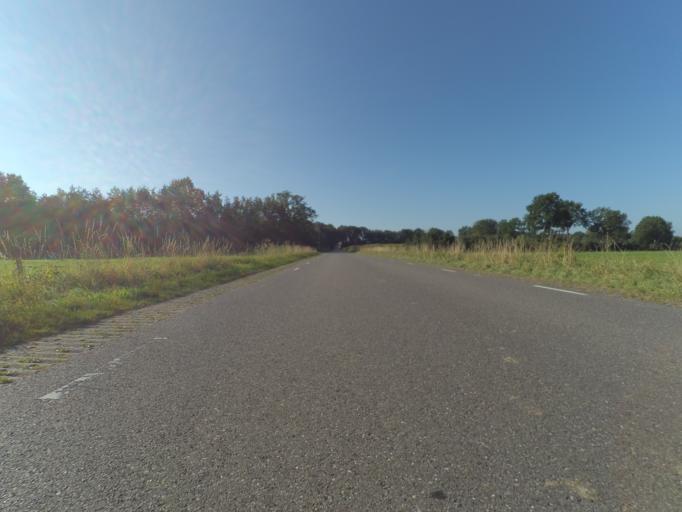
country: NL
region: Gelderland
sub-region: Gemeente Putten
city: Putten
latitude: 52.2309
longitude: 5.5757
